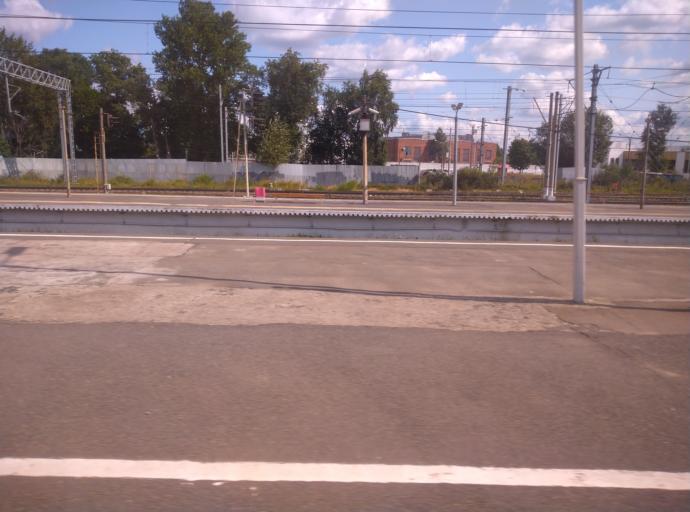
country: RU
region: St.-Petersburg
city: Obukhovo
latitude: 59.8486
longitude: 30.4544
